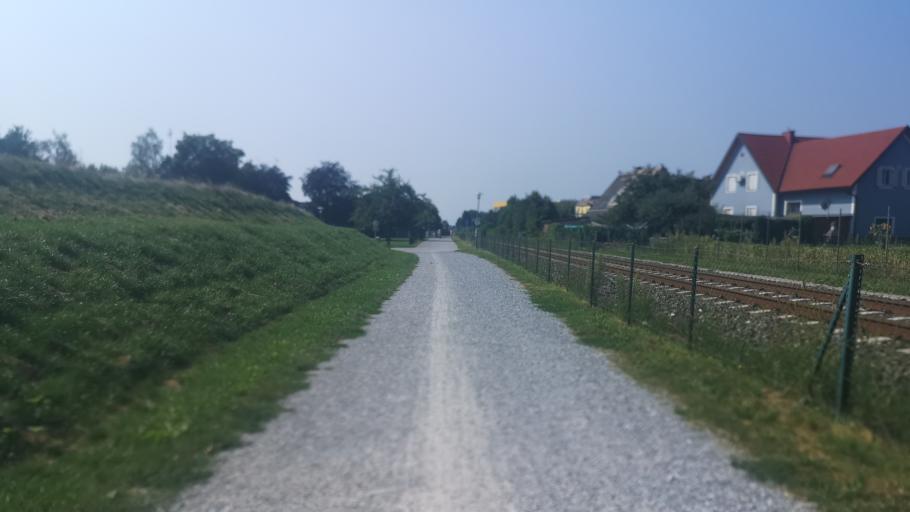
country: AT
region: Styria
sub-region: Politischer Bezirk Graz-Umgebung
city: Seiersberg
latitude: 47.0128
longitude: 15.4035
